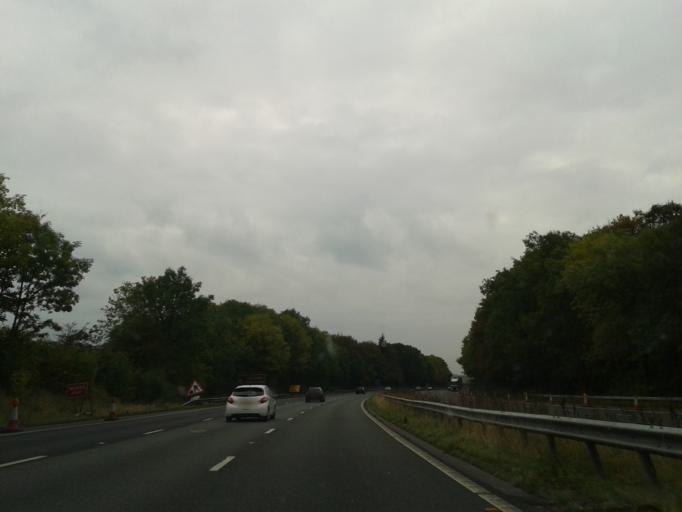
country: GB
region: England
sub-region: Lancashire
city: Bolton le Sands
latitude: 54.0847
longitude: -2.7667
